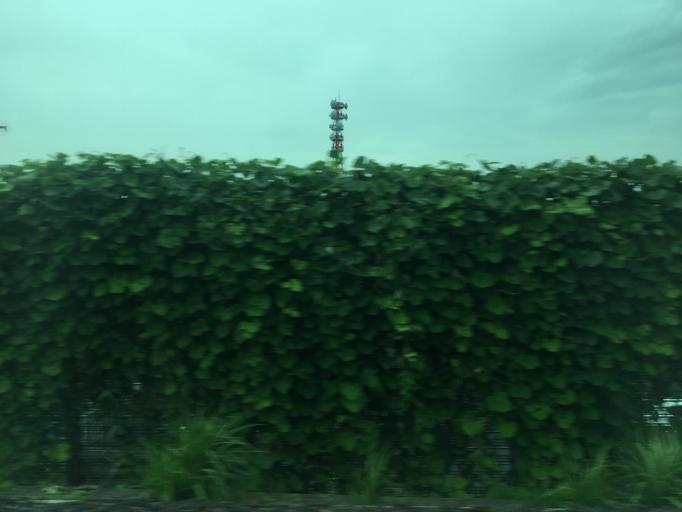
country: JP
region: Saitama
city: Kurihashi
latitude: 36.1442
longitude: 139.6961
